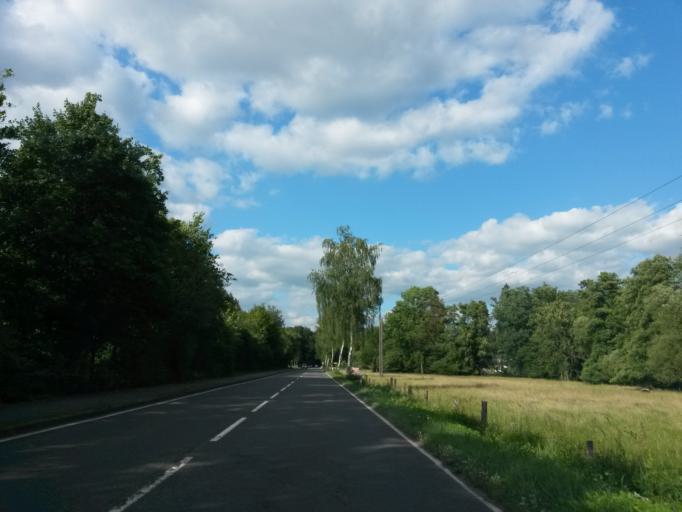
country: DE
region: North Rhine-Westphalia
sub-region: Regierungsbezirk Koln
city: Ruppichteroth
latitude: 50.8494
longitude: 7.5033
